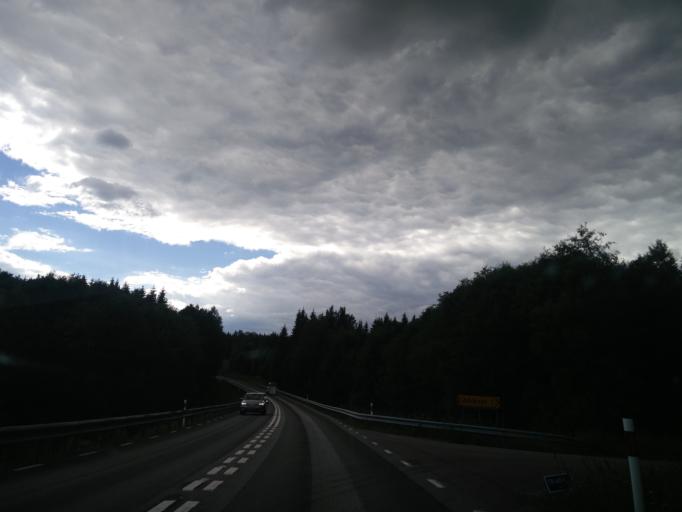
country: SE
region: Vaermland
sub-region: Filipstads Kommun
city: Filipstad
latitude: 59.7888
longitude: 14.3131
